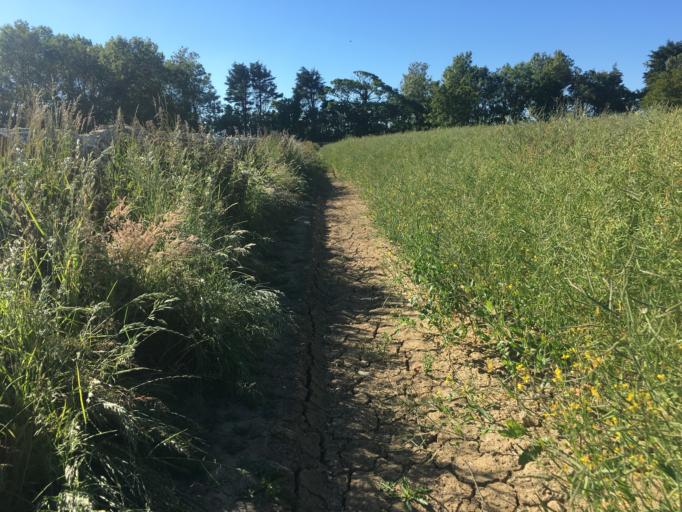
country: GB
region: England
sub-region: Northumberland
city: North Sunderland
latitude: 55.5656
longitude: -1.6501
